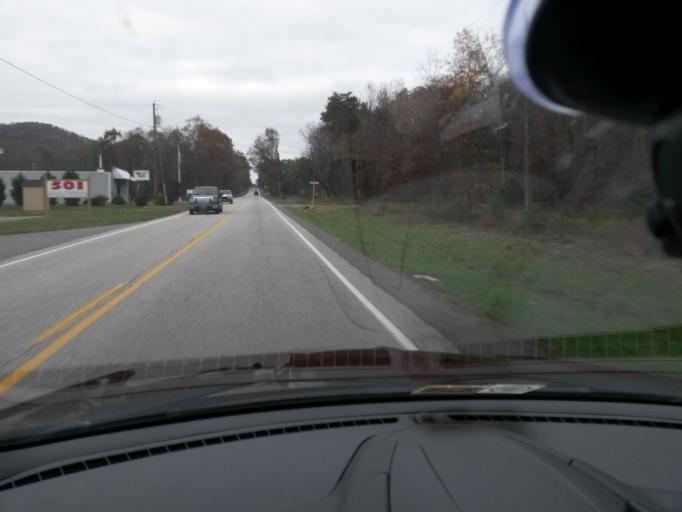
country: US
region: Virginia
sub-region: Rockbridge County
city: Glasgow
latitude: 37.6553
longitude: -79.4246
